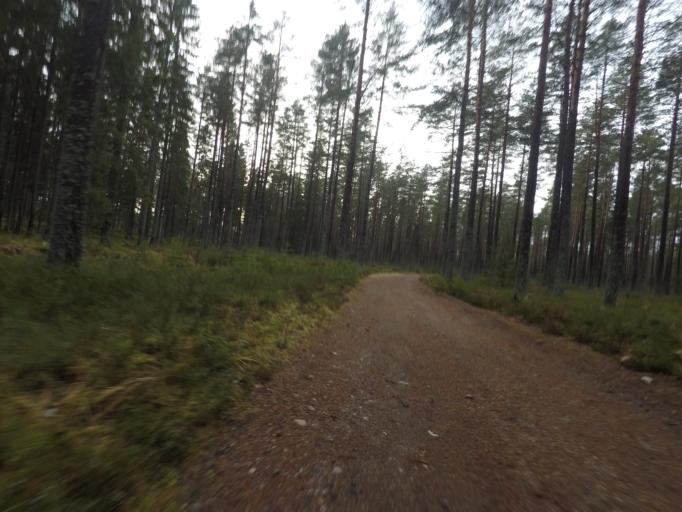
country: SE
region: Vaestmanland
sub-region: Kungsors Kommun
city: Kungsoer
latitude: 59.3595
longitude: 16.1179
